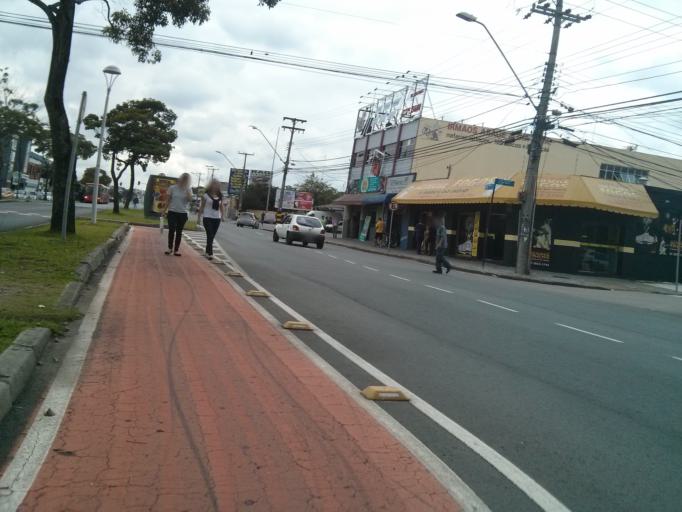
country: BR
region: Parana
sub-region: Curitiba
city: Curitiba
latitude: -25.4742
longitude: -49.2508
